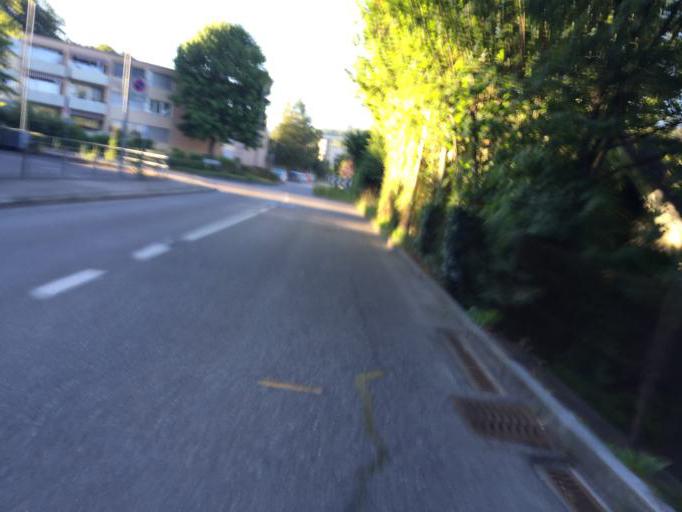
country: CH
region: Bern
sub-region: Bern-Mittelland District
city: Bern
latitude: 46.9734
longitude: 7.4328
